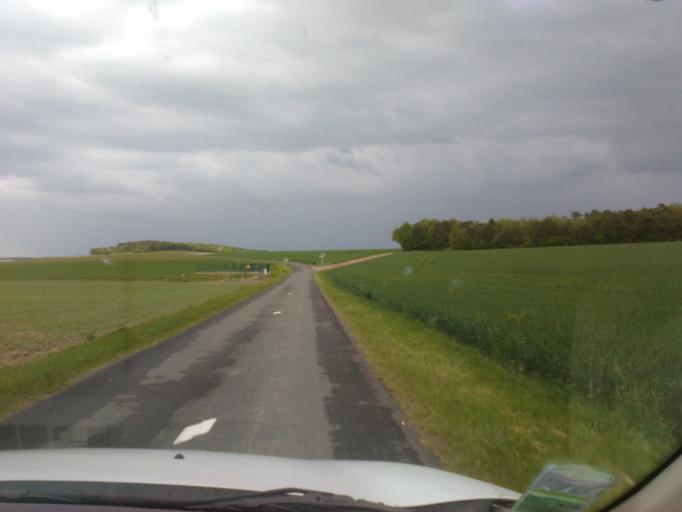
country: FR
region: Bourgogne
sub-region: Departement de l'Yonne
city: Thorigny-sur-Oreuse
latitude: 48.3751
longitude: 3.4735
